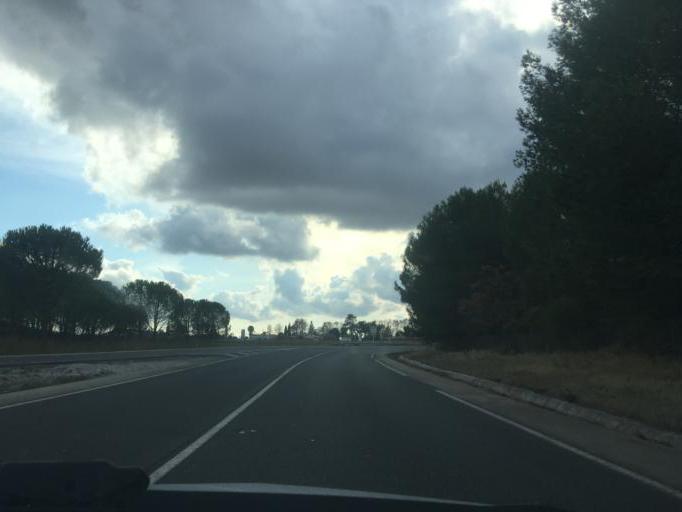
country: FR
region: Provence-Alpes-Cote d'Azur
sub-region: Departement du Var
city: Cuers
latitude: 43.2482
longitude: 6.0925
